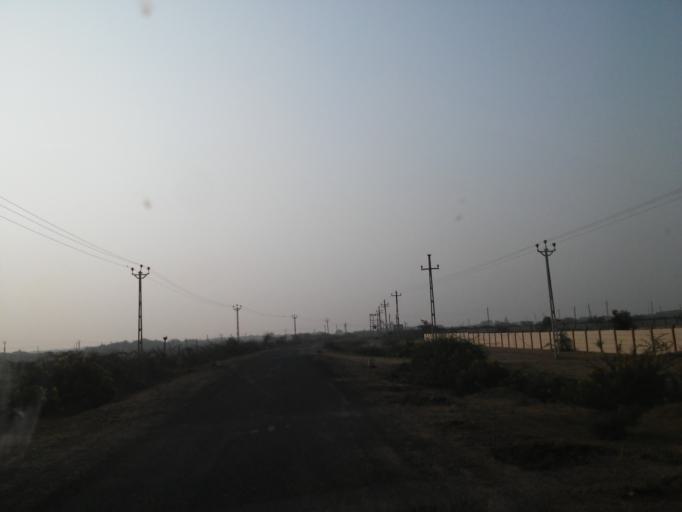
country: IN
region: Gujarat
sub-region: Kachchh
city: Mandvi
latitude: 22.8215
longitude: 69.3890
